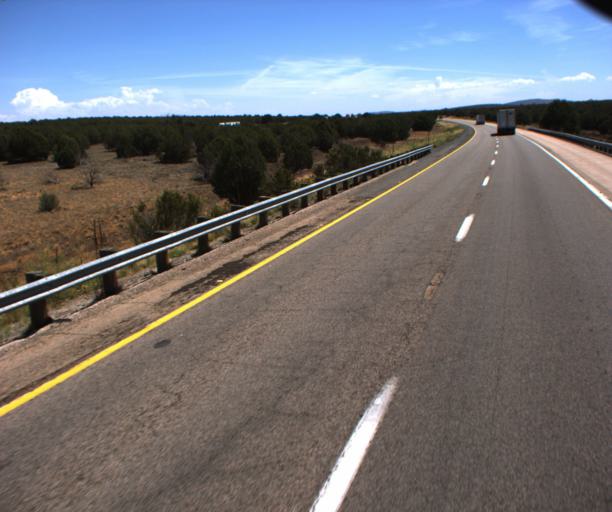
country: US
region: Arizona
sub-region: Mohave County
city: Peach Springs
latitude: 35.2073
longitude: -113.2750
